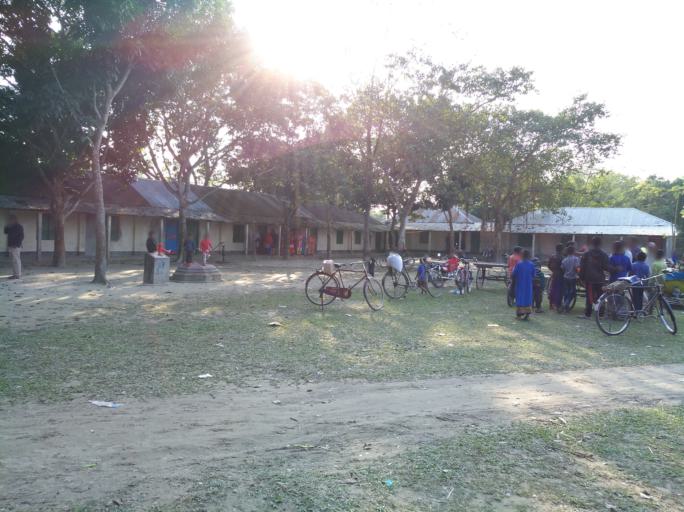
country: BD
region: Rajshahi
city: Saidpur
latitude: 25.9660
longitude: 88.7717
